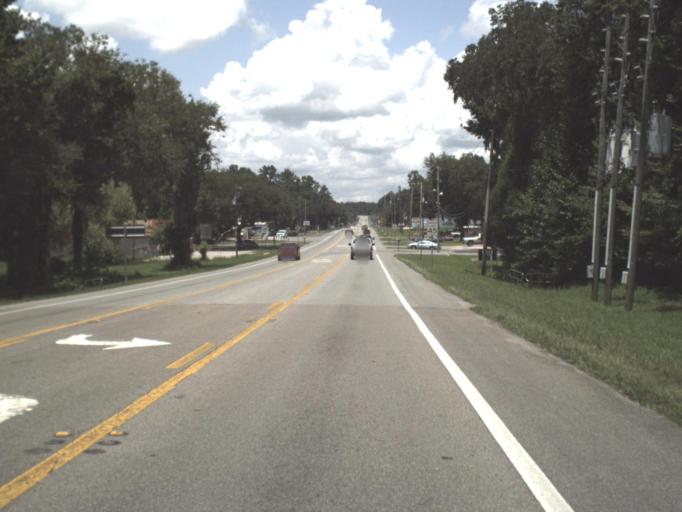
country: US
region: Florida
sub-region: Hernando County
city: Brooksville
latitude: 28.5575
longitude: -82.3976
